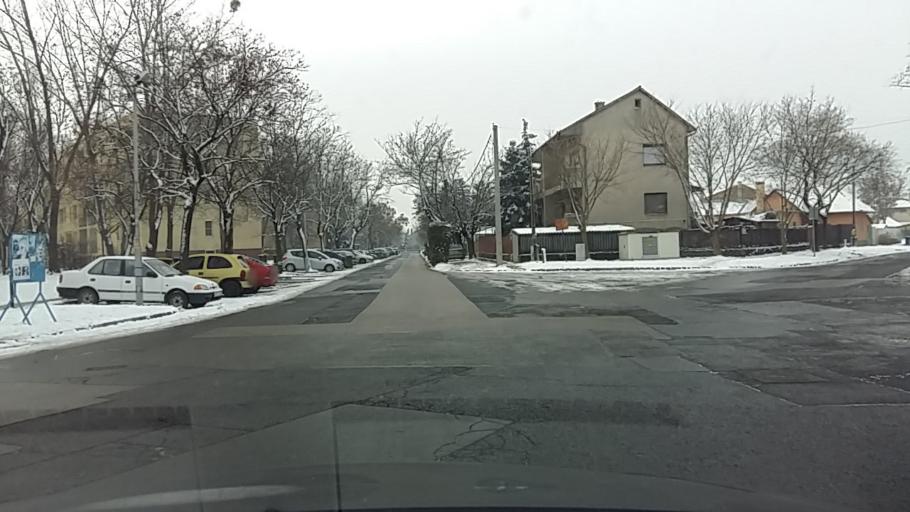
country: HU
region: Budapest
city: Budapest XIX. keruelet
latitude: 47.4384
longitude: 19.1336
